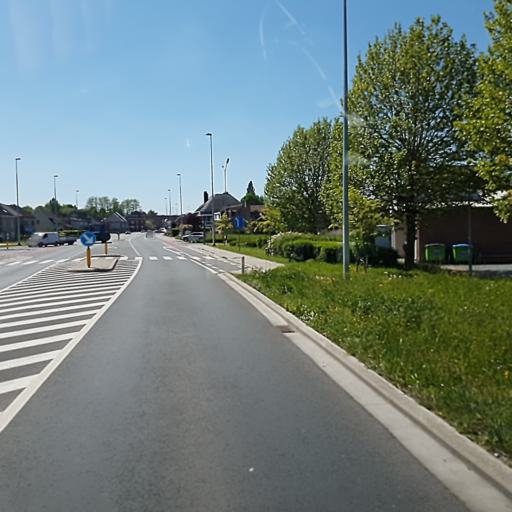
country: BE
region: Flanders
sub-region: Provincie Oost-Vlaanderen
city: Lede
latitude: 50.9349
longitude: 3.9735
